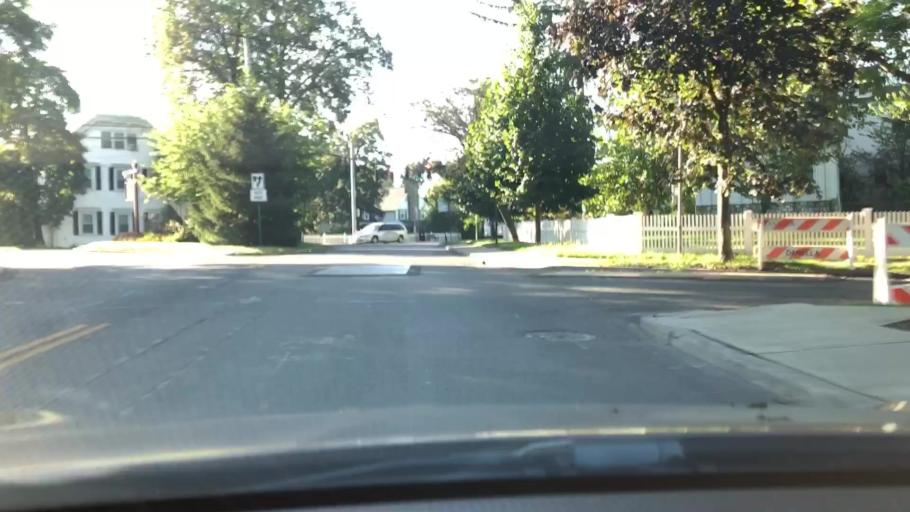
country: US
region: New York
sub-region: Westchester County
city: Tuckahoe
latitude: 40.9463
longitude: -73.8209
